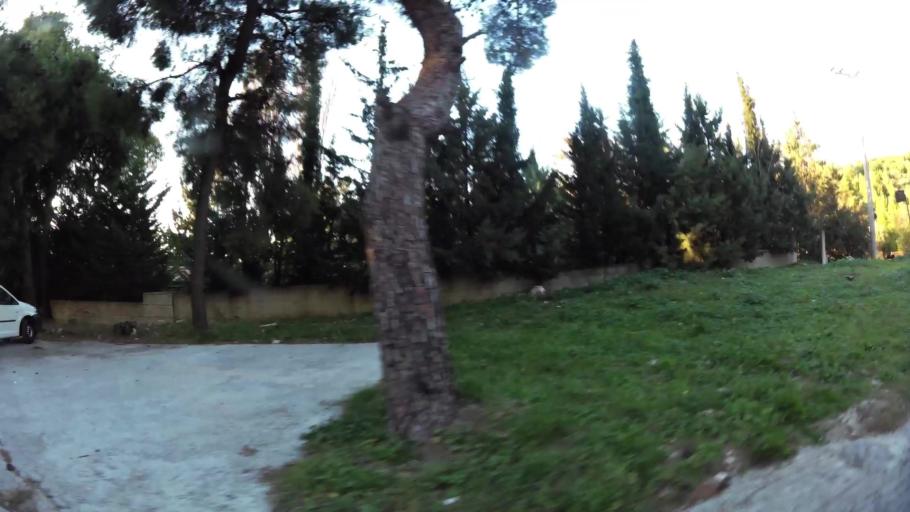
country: GR
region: Attica
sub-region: Nomarchia Athinas
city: Penteli
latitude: 38.0513
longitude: 23.8612
